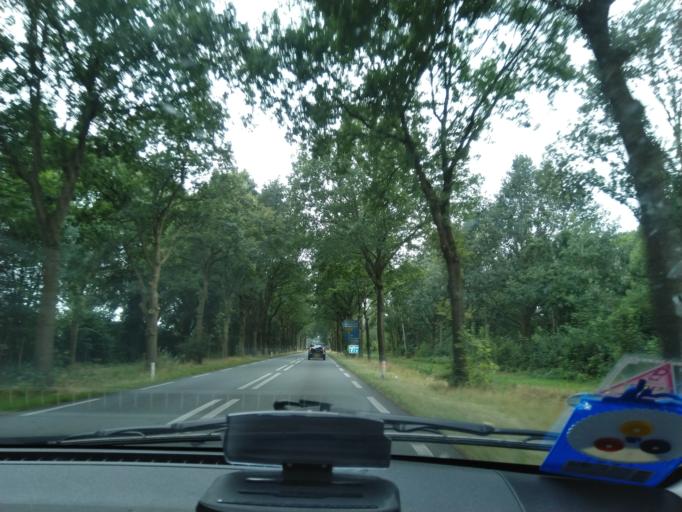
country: NL
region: Groningen
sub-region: Gemeente Pekela
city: Oude Pekela
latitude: 53.1100
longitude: 7.0084
